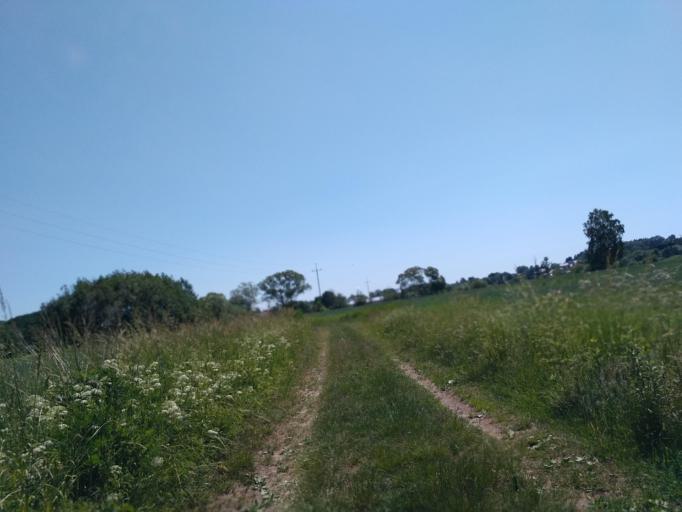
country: PL
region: Subcarpathian Voivodeship
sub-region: Krosno
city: Krosno
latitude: 49.7167
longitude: 21.7758
